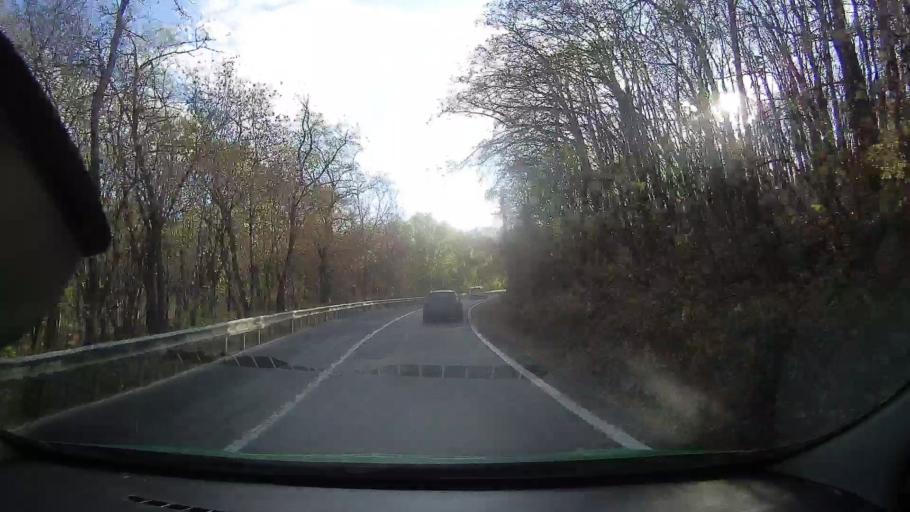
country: RO
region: Tulcea
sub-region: Comuna Topolog
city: Topolog
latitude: 44.9119
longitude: 28.4195
